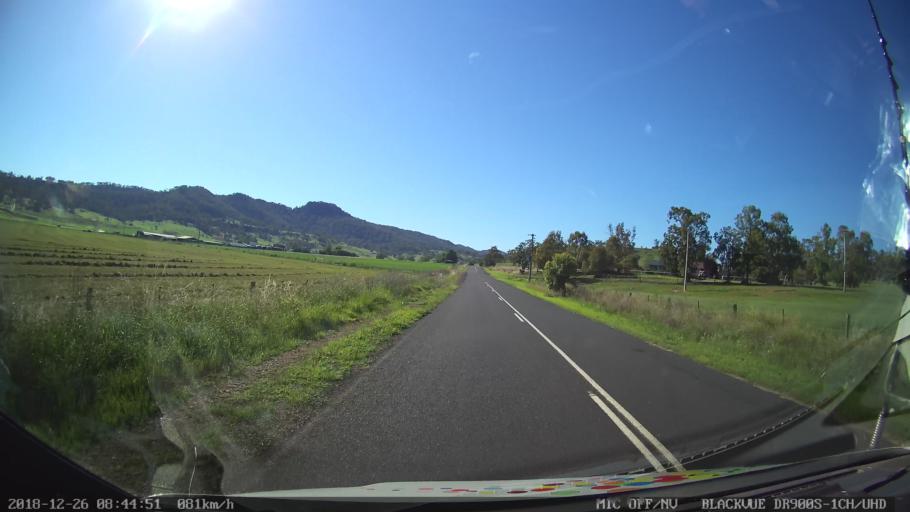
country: AU
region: New South Wales
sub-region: Mid-Western Regional
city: Kandos
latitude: -32.5195
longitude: 150.0818
